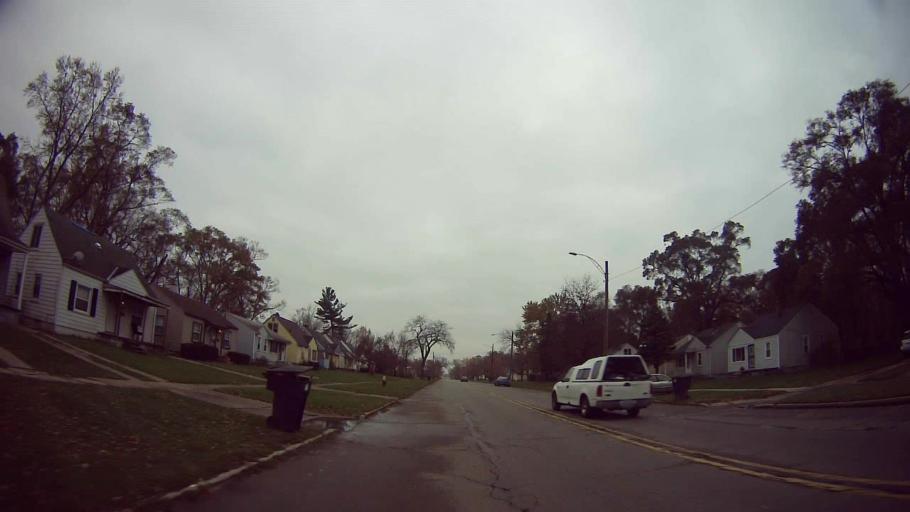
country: US
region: Michigan
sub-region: Wayne County
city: Redford
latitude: 42.4070
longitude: -83.2570
